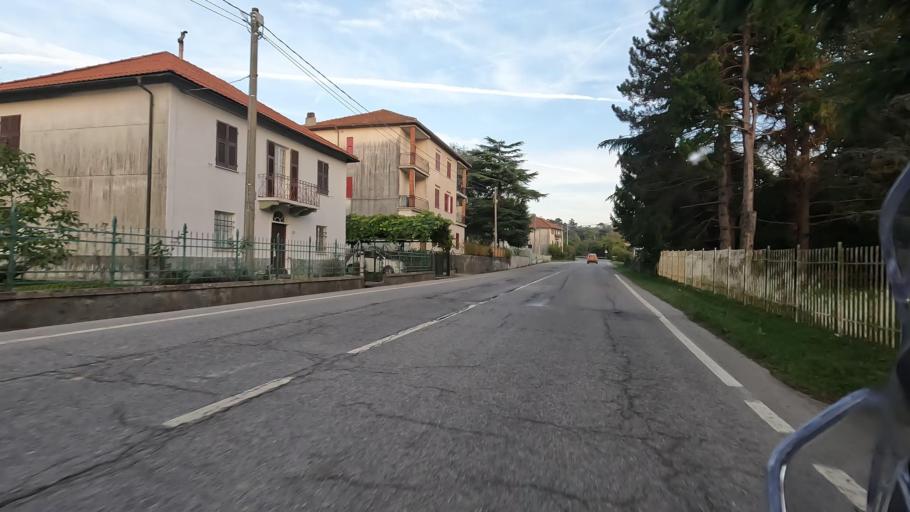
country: IT
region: Liguria
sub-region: Provincia di Savona
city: Osteria dei Cacciatori-Stella
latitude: 44.4296
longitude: 8.4678
